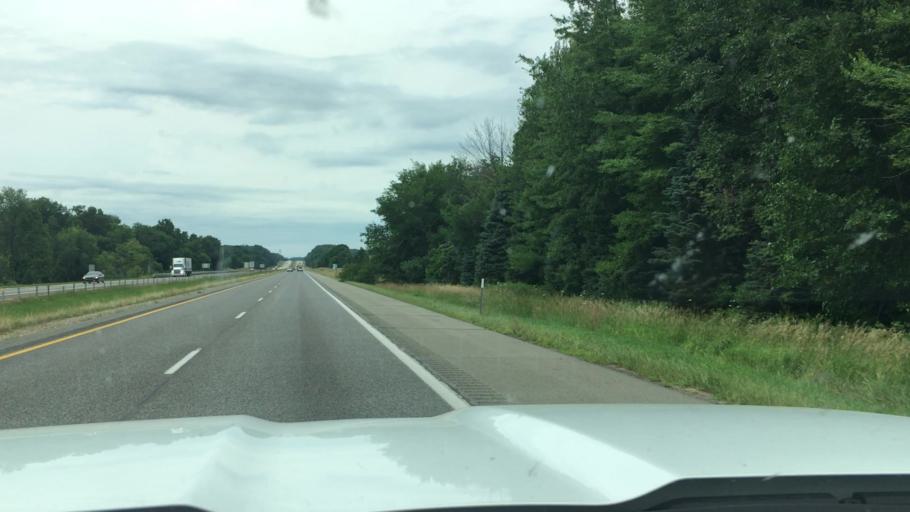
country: US
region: Michigan
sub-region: Allegan County
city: Otsego
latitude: 42.5247
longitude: -85.6578
